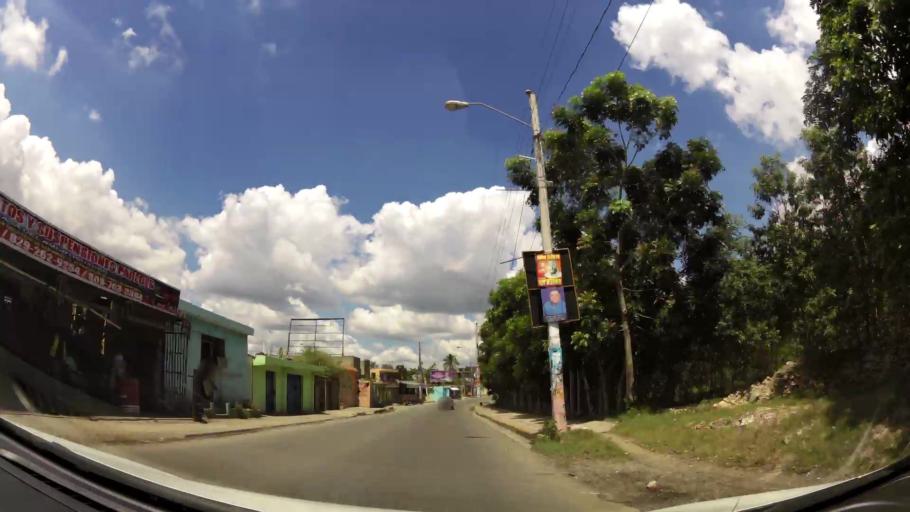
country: DO
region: Santo Domingo
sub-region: Santo Domingo
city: Santo Domingo Este
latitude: 18.5216
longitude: -69.8686
